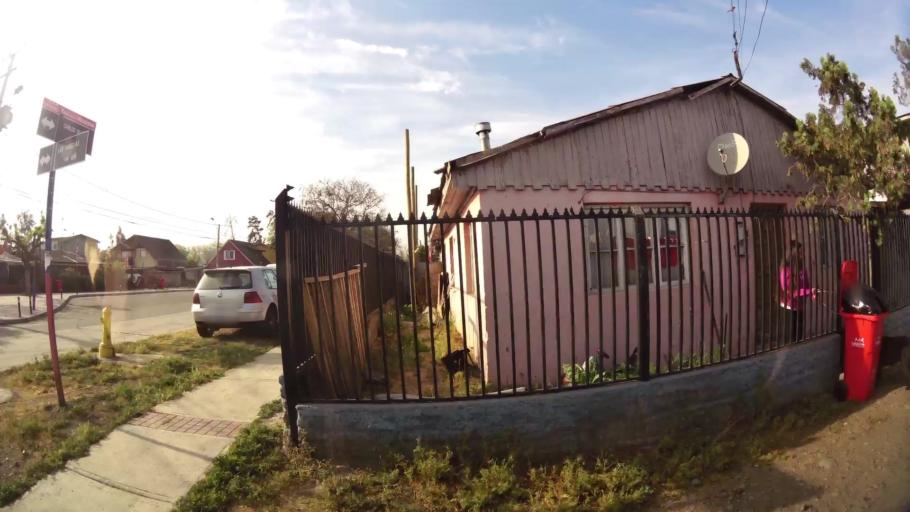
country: CL
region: Santiago Metropolitan
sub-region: Provincia de Talagante
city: Talagante
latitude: -33.6699
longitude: -70.9340
